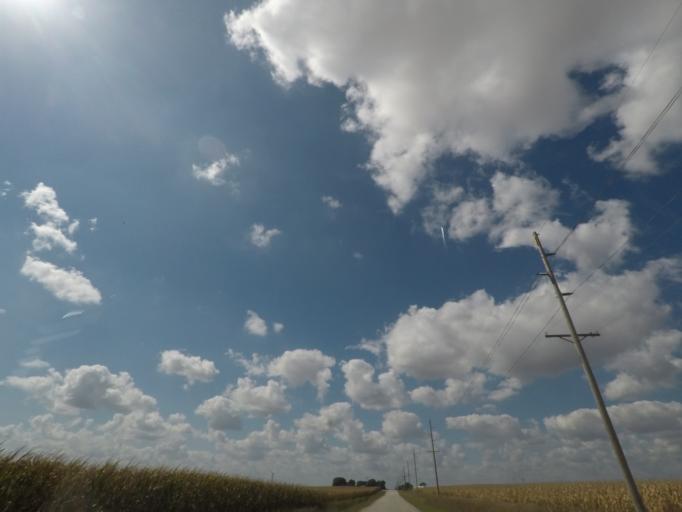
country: US
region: Iowa
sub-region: Story County
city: Nevada
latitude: 42.0344
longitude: -93.4020
